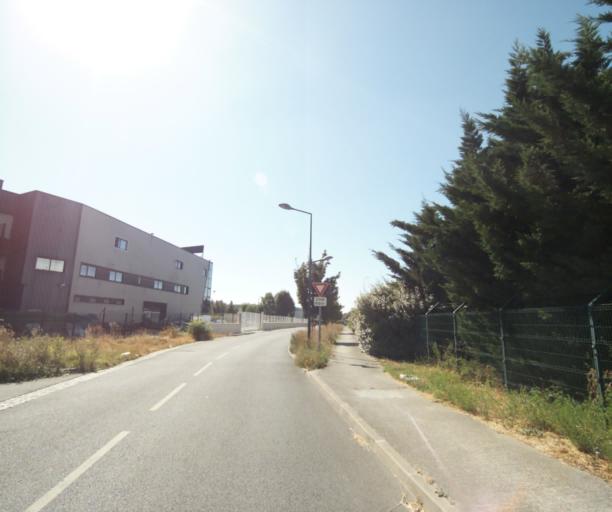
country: FR
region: Ile-de-France
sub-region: Departement des Hauts-de-Seine
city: Villeneuve-la-Garenne
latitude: 48.9274
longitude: 2.3206
